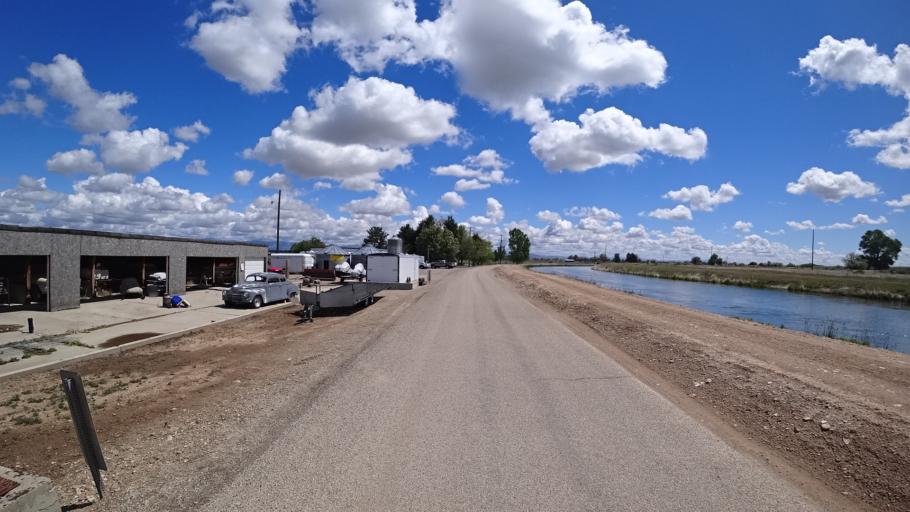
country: US
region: Idaho
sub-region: Ada County
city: Kuna
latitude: 43.4601
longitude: -116.3663
